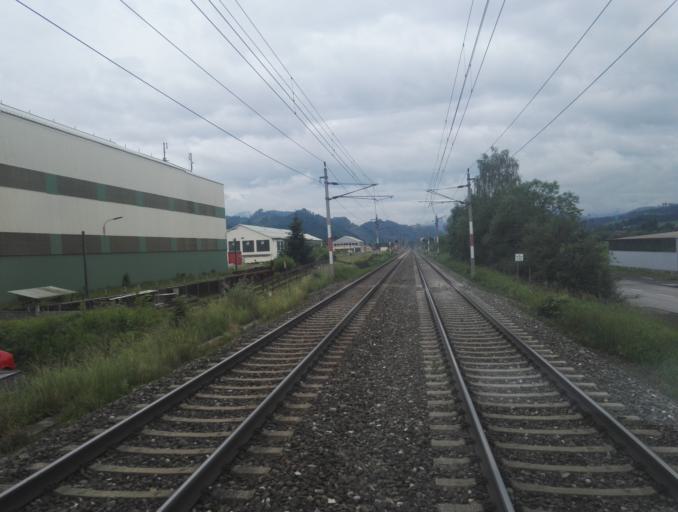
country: AT
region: Styria
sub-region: Politischer Bezirk Bruck-Muerzzuschlag
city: Frauenberg
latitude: 47.4581
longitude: 15.3373
